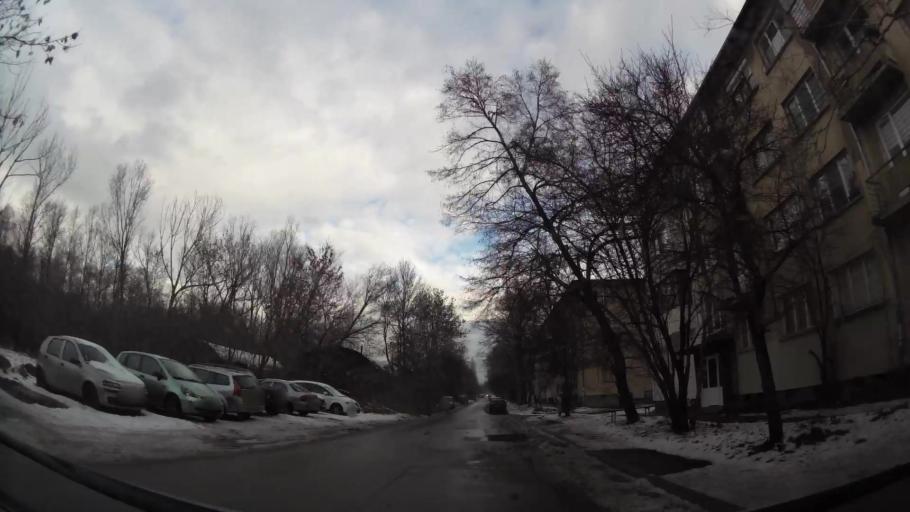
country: BG
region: Sofia-Capital
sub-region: Stolichna Obshtina
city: Sofia
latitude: 42.7054
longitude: 23.2755
